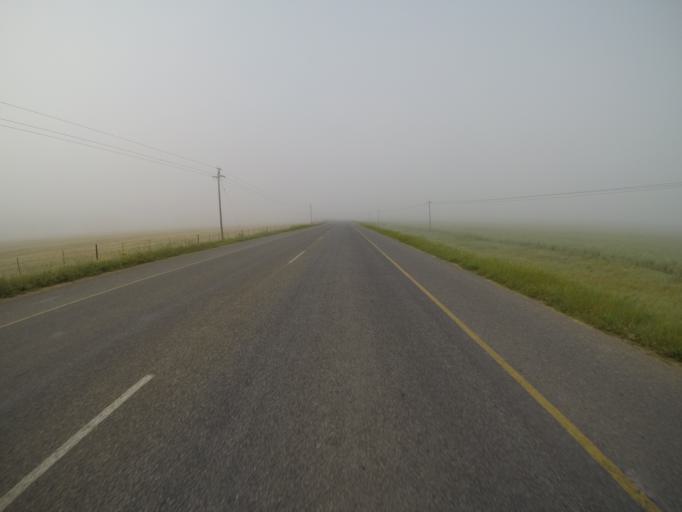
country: ZA
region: Western Cape
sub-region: City of Cape Town
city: Kraaifontein
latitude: -33.6767
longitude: 18.7065
